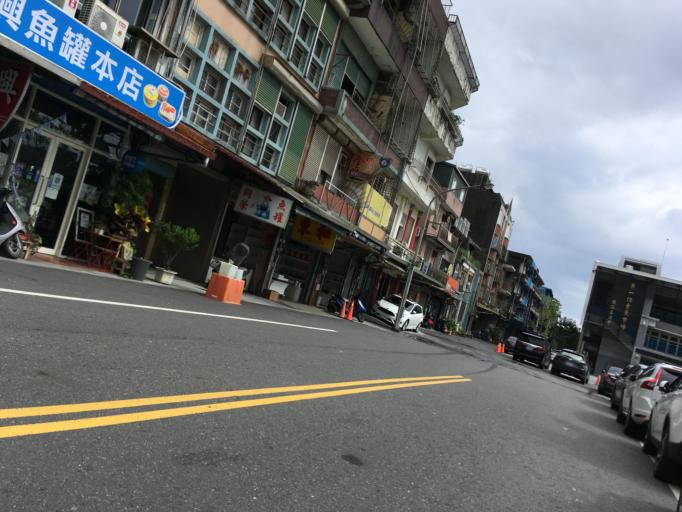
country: TW
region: Taiwan
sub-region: Yilan
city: Yilan
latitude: 24.5825
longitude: 121.8679
